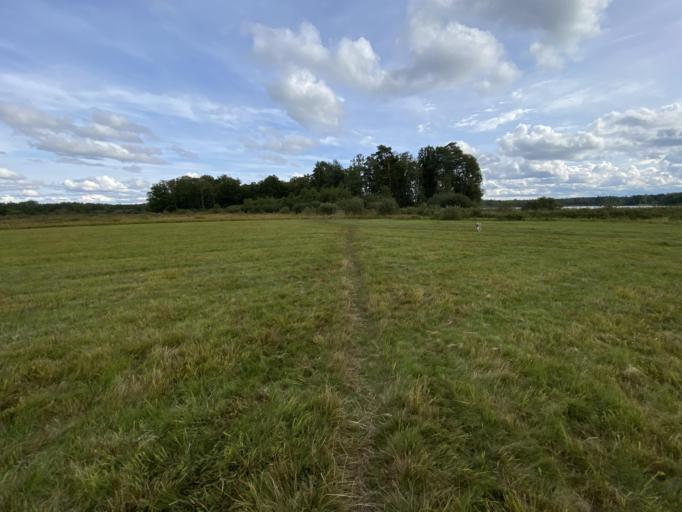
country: SE
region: Skane
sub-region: Hassleholms Kommun
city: Hastveda
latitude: 56.3618
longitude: 13.8849
